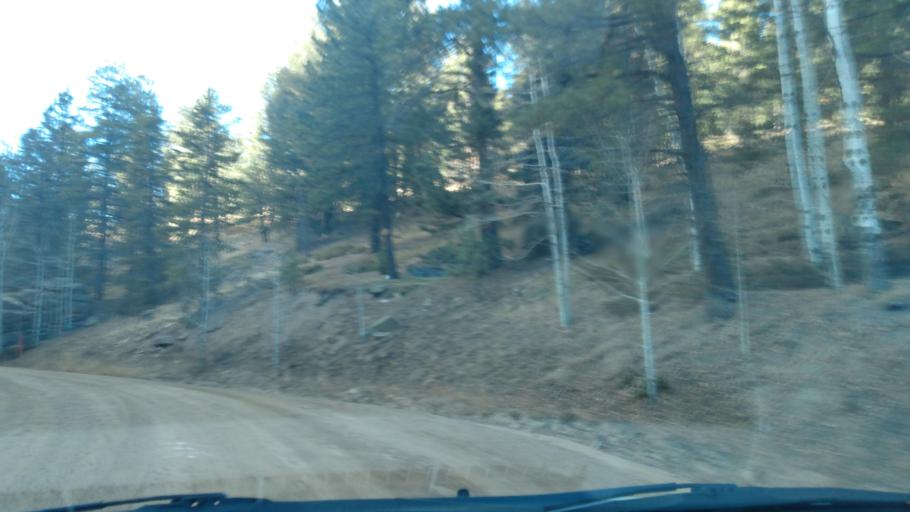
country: US
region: Colorado
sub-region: Boulder County
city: Nederland
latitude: 39.9449
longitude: -105.4454
